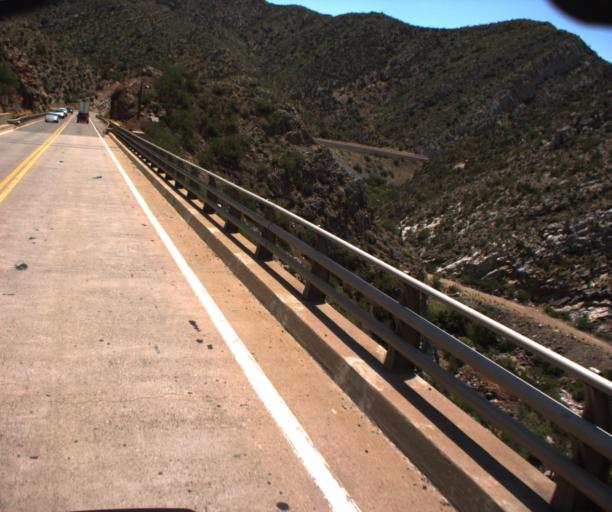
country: US
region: Arizona
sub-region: Pinal County
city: Superior
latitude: 33.2986
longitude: -111.0899
